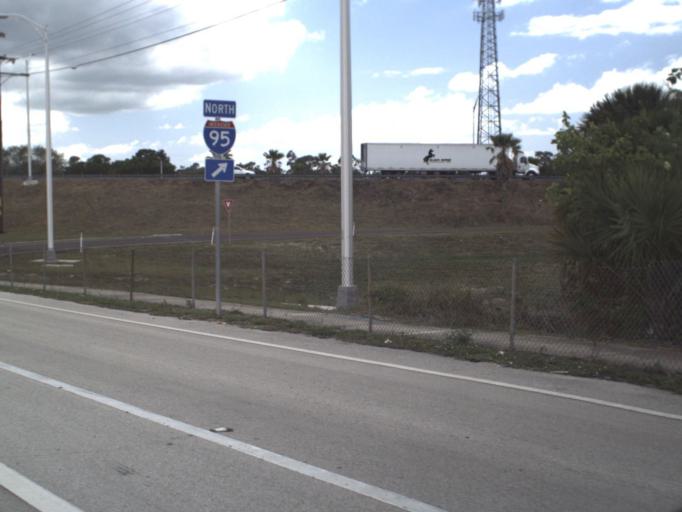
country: US
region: Florida
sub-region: Brevard County
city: Titusville
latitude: 28.6170
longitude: -80.8500
